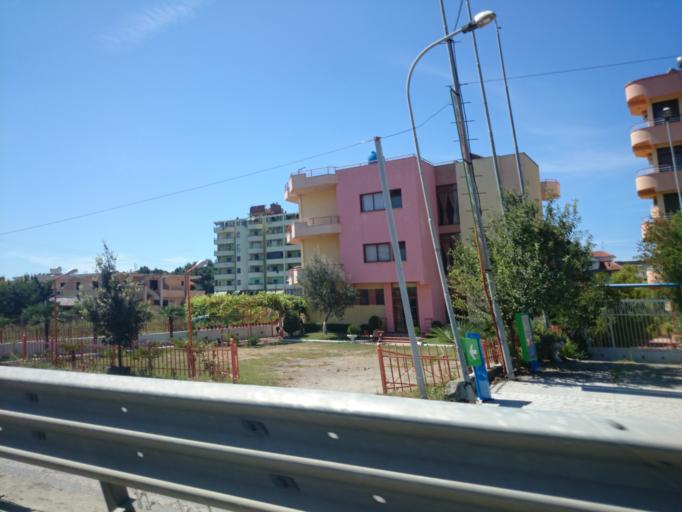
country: AL
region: Tirane
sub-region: Rrethi i Kavajes
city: Golem
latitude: 41.2627
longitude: 19.5245
